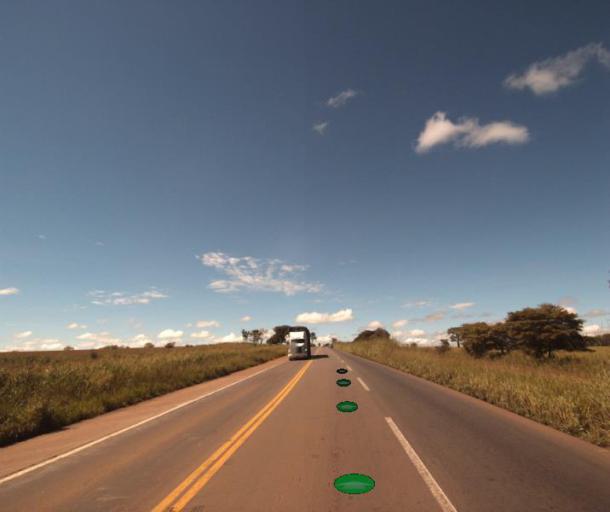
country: BR
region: Goias
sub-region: Rialma
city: Rialma
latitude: -15.3518
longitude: -49.5676
